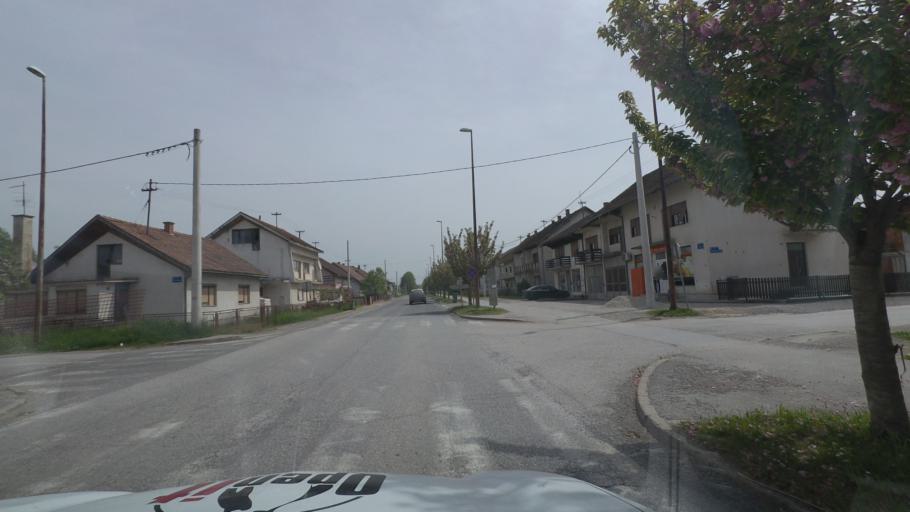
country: HR
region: Sisacko-Moslavacka
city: Glina
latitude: 45.3334
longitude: 16.0899
